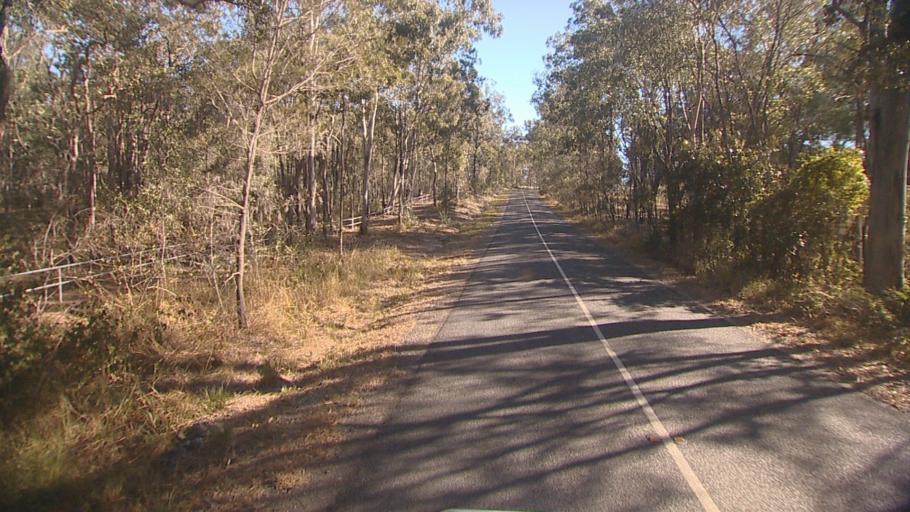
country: AU
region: Queensland
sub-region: Gold Coast
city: Ormeau Hills
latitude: -27.8208
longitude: 153.1698
